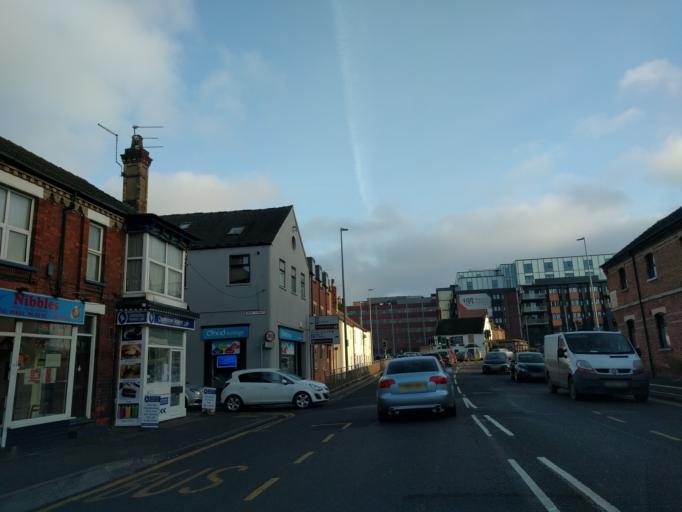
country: GB
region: England
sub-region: Lincolnshire
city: Lincoln
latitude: 53.2310
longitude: -0.5494
